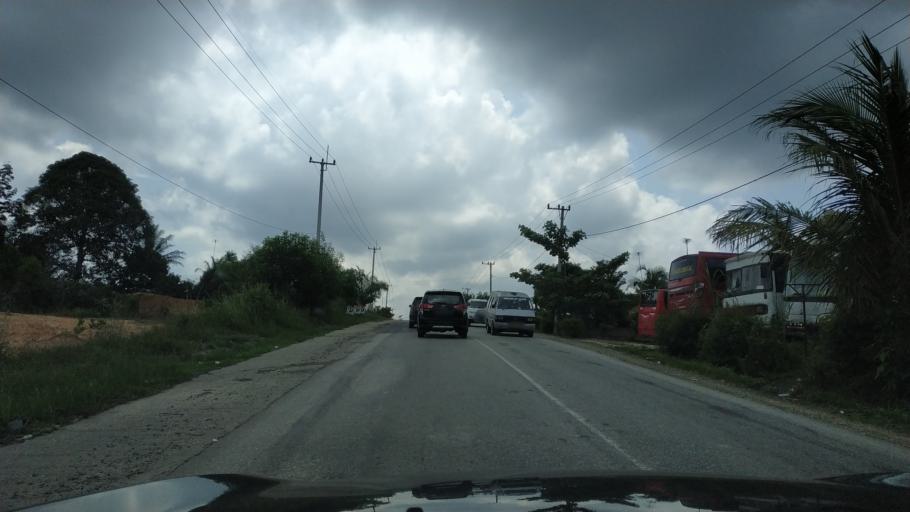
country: ID
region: Riau
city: Pangkalanbunut
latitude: 0.3030
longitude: 101.9133
